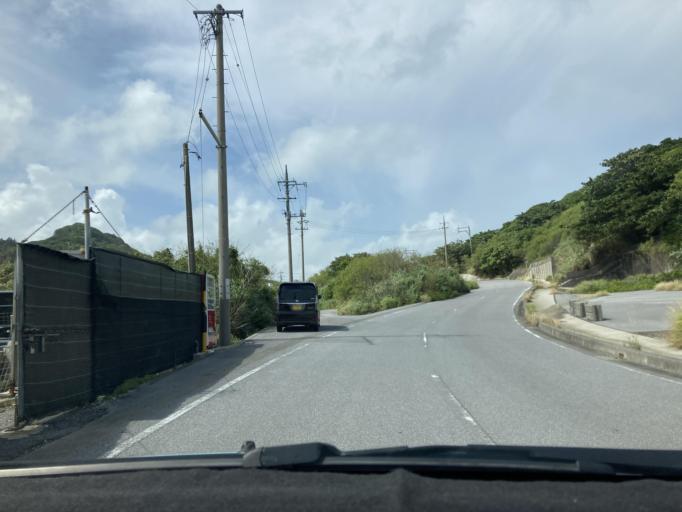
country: JP
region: Okinawa
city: Ginowan
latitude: 26.1869
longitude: 127.8215
